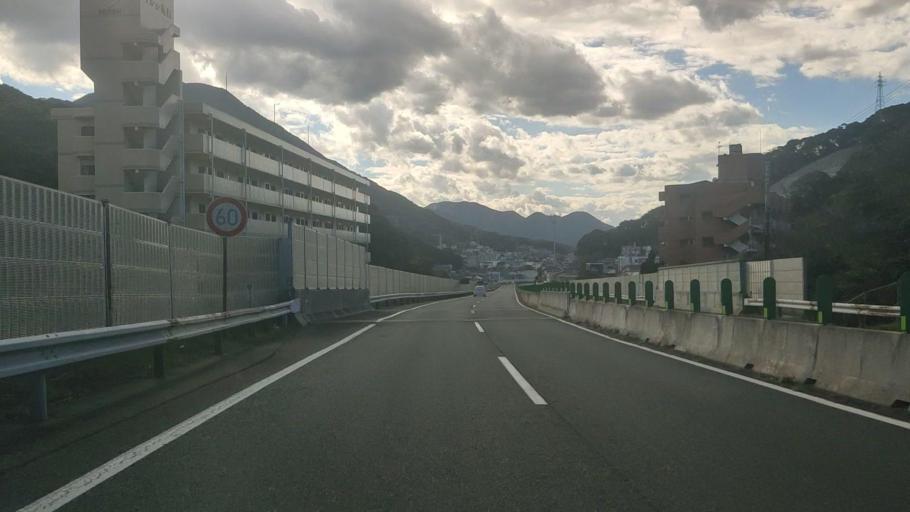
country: JP
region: Yamaguchi
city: Shimonoseki
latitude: 33.9132
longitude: 130.9599
